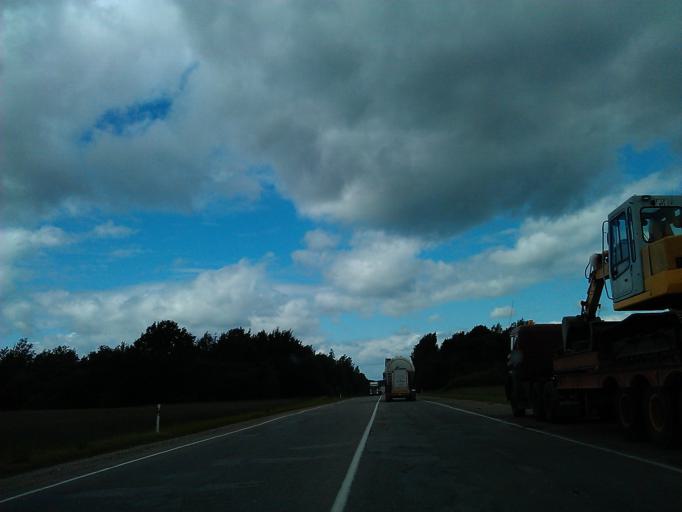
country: LV
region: Tukuma Rajons
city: Tukums
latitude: 56.9333
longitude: 23.1990
